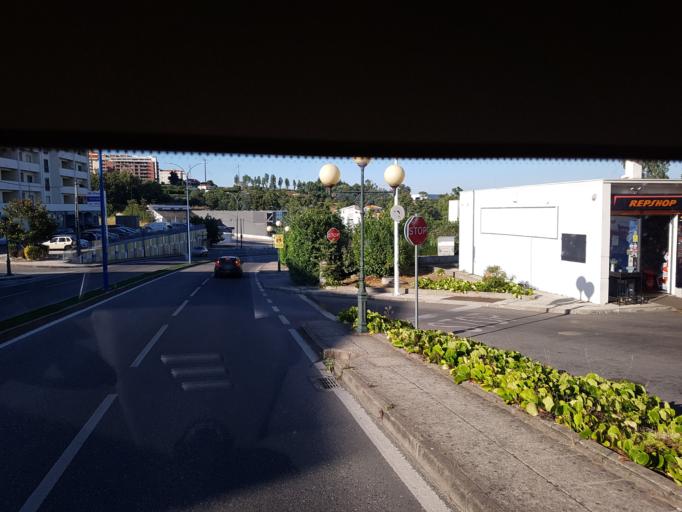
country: PT
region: Castelo Branco
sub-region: Covilha
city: Covilha
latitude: 40.2668
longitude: -7.5000
